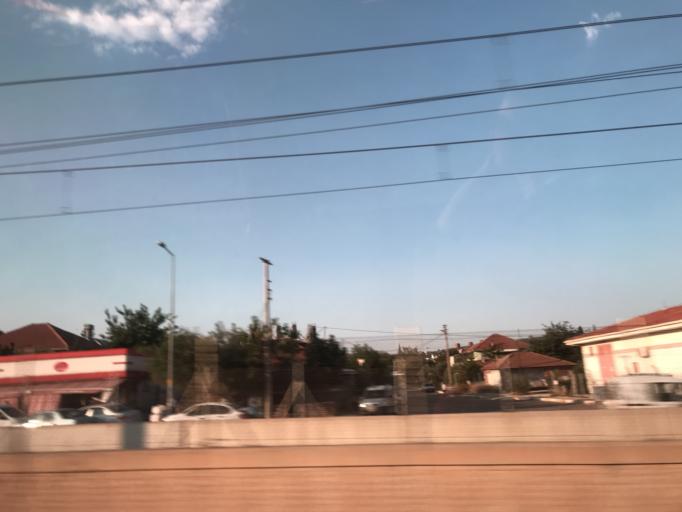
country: TR
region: Antalya
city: Antalya
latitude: 36.9369
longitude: 30.6541
